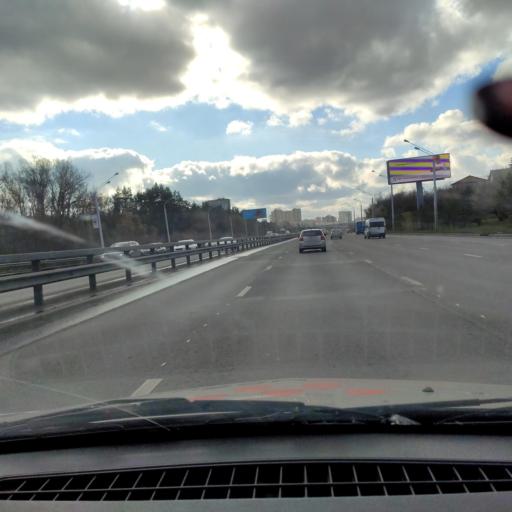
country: RU
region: Bashkortostan
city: Ufa
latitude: 54.7354
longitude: 56.0047
